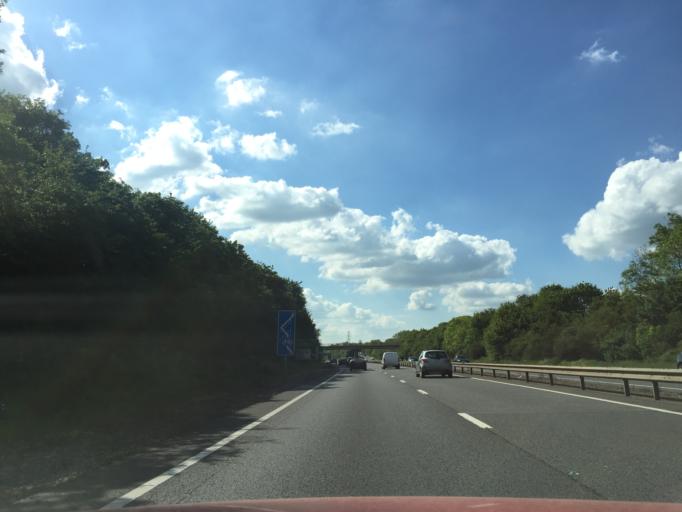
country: GB
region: England
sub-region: Milton Keynes
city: Bradwell
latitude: 52.0449
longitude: -0.7953
